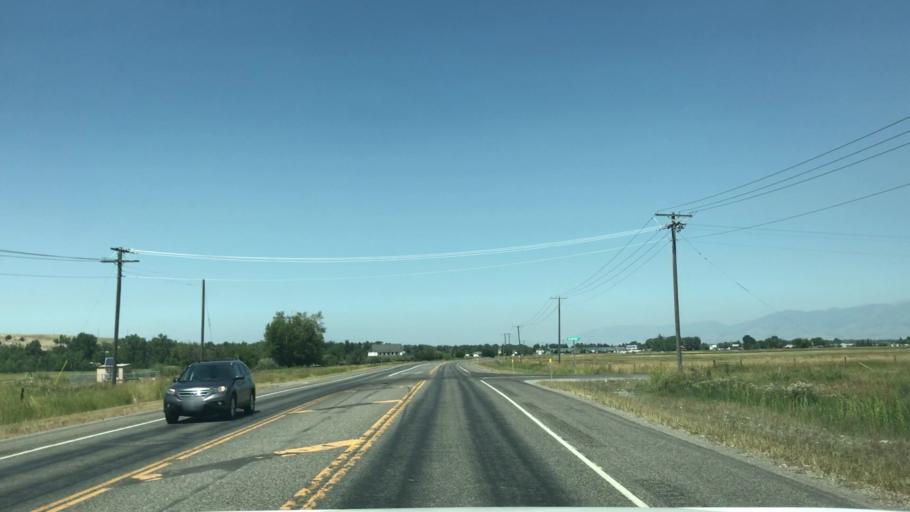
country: US
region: Montana
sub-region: Gallatin County
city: Four Corners
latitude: 45.6377
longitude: -111.1967
